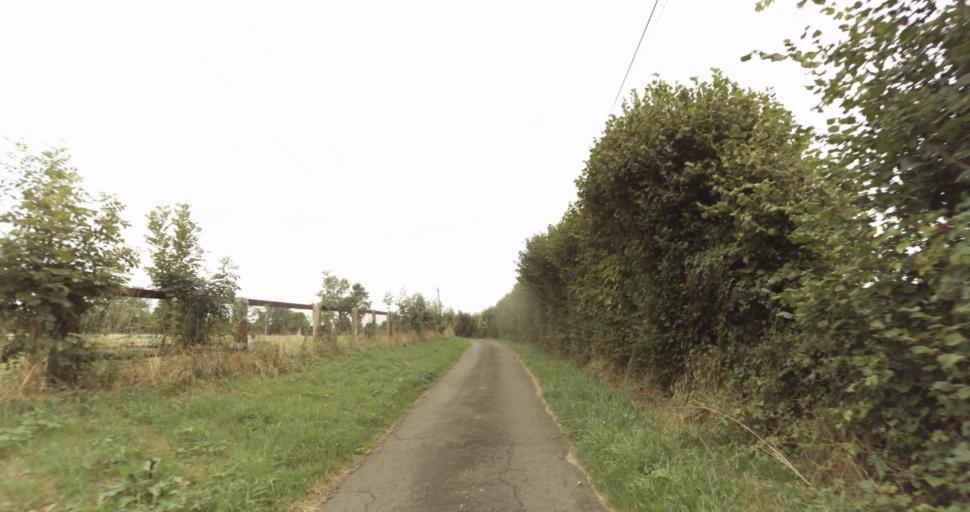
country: FR
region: Lower Normandy
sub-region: Departement de l'Orne
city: Sainte-Gauburge-Sainte-Colombe
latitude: 48.7240
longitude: 0.3499
